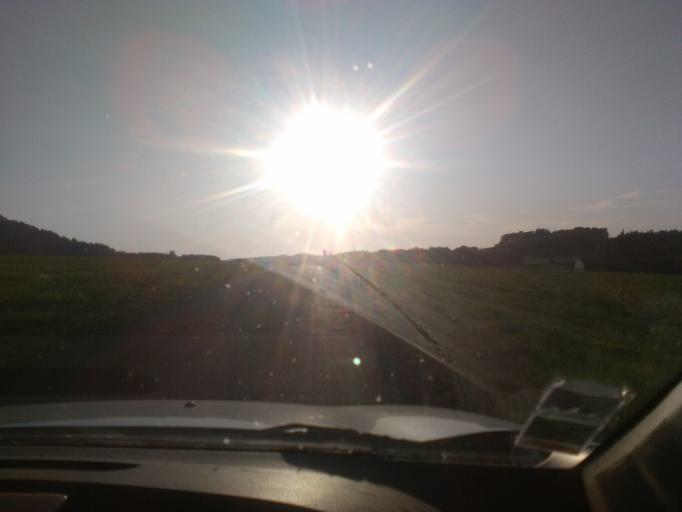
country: FR
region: Lorraine
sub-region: Departement des Vosges
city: Saint-Michel-sur-Meurthe
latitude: 48.3215
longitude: 6.8686
